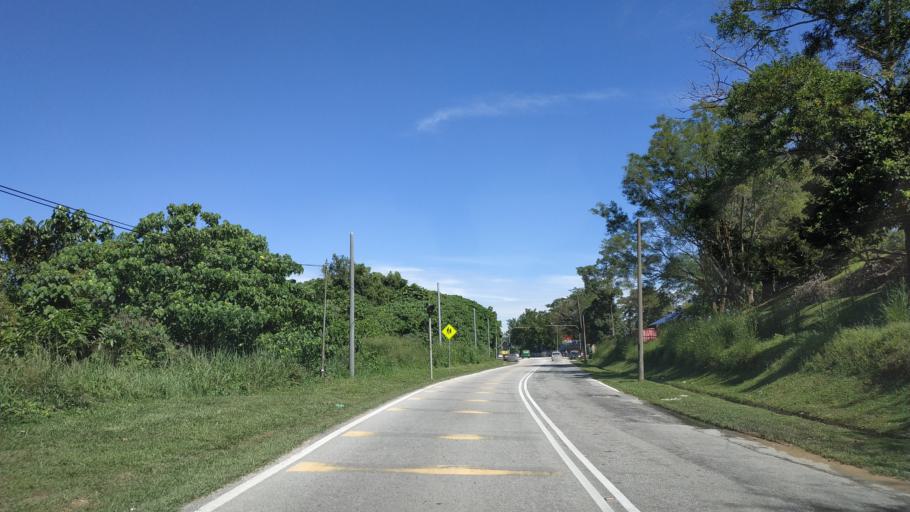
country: MY
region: Kedah
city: Kulim
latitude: 5.3401
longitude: 100.5375
